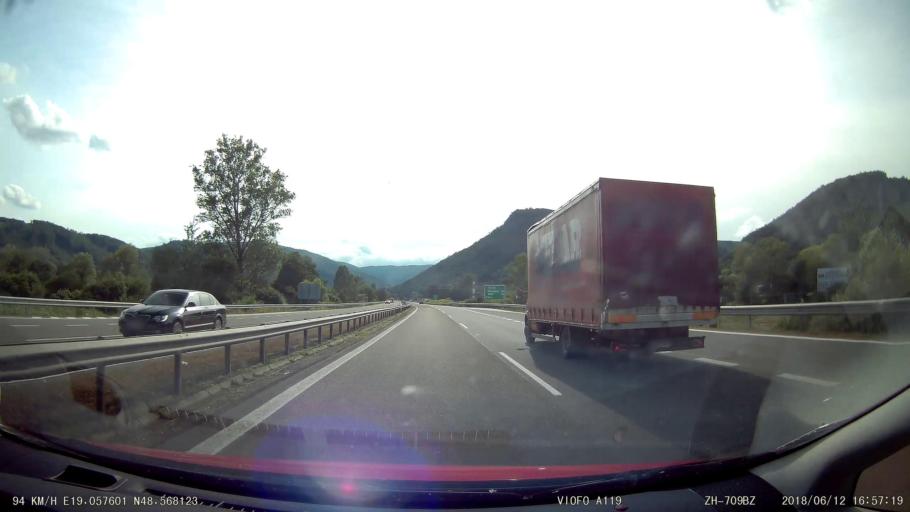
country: SK
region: Banskobystricky
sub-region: Okres Banska Bystrica
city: Zvolen
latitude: 48.5674
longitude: 19.0585
